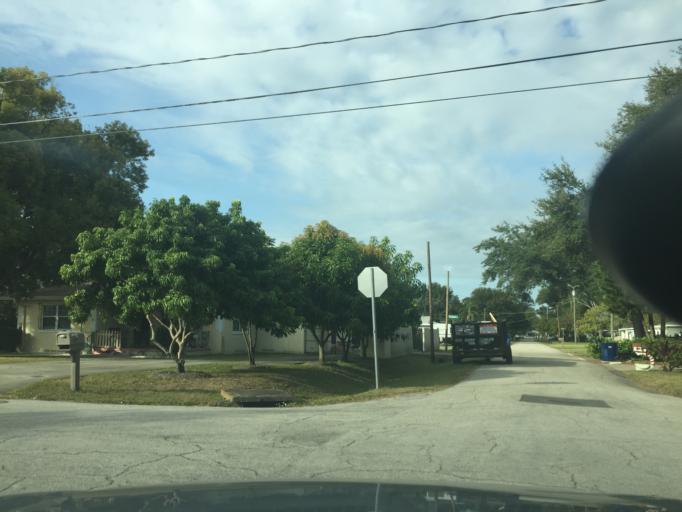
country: US
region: Florida
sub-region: Hillsborough County
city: Tampa
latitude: 27.9484
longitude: -82.4913
